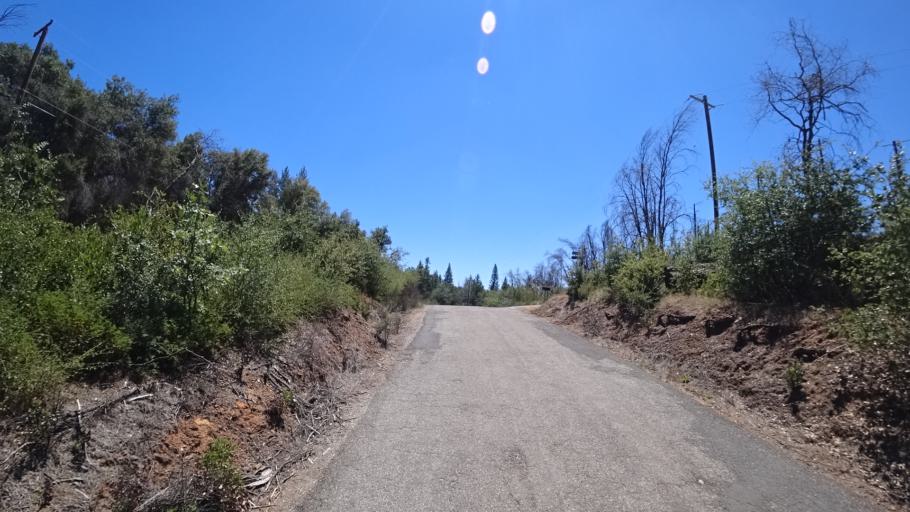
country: US
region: California
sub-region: Calaveras County
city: Mountain Ranch
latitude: 38.2382
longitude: -120.5464
